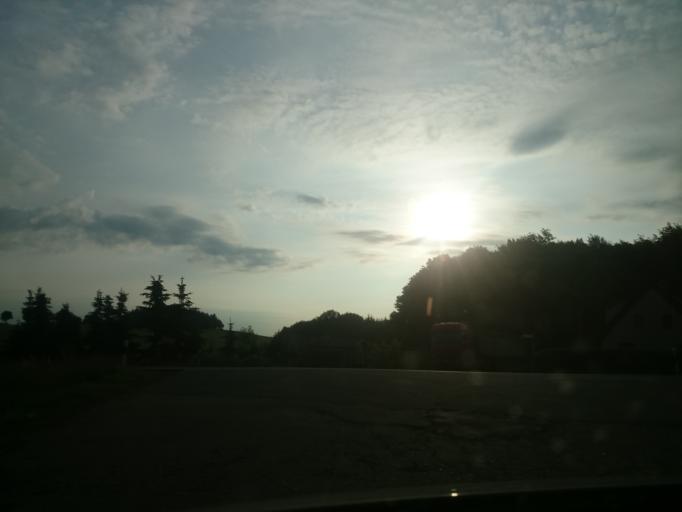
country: DE
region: Saxony
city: Grossolbersdorf
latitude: 50.7164
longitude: 13.0993
